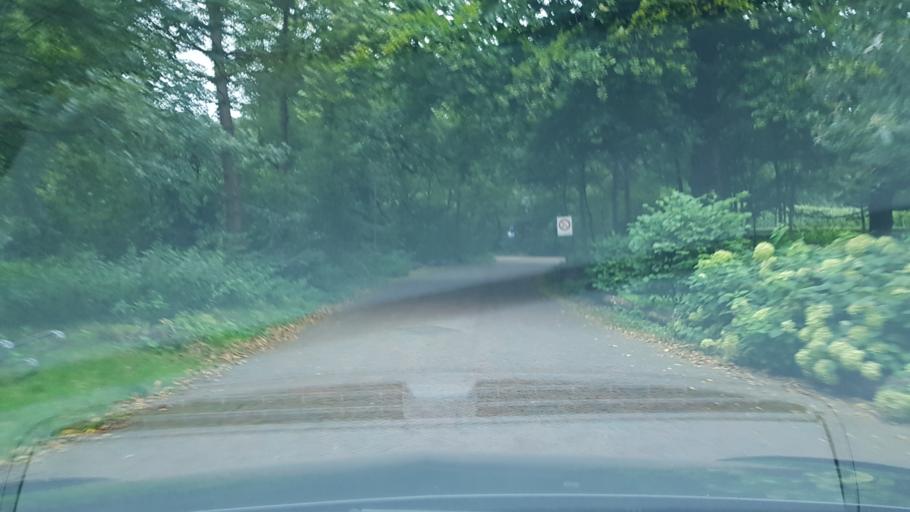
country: NL
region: North Holland
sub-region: Gemeente Heemstede
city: Heemstede
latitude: 52.3379
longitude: 4.6140
